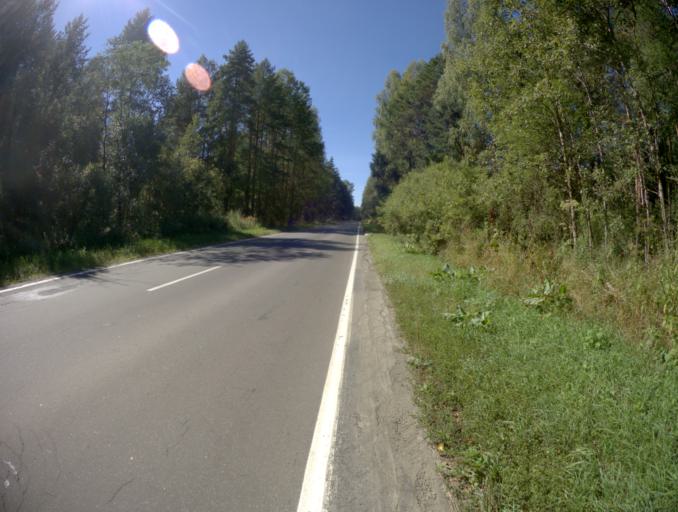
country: RU
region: Vladimir
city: Zolotkovo
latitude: 55.6185
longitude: 40.9900
